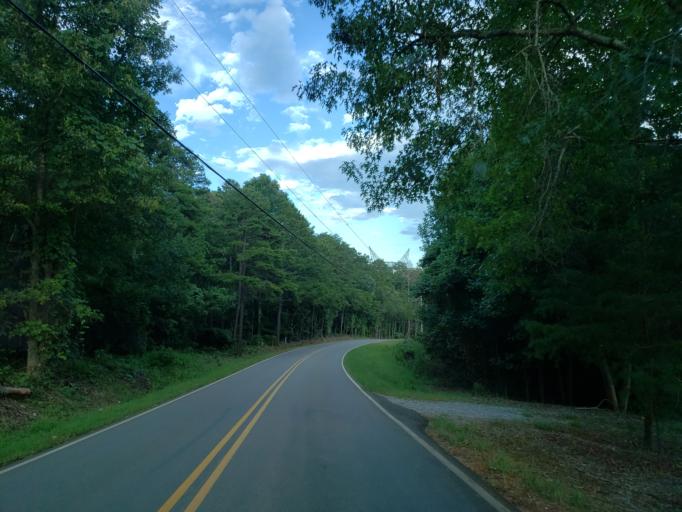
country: US
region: Georgia
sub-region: Cherokee County
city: Ball Ground
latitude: 34.3273
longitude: -84.4292
